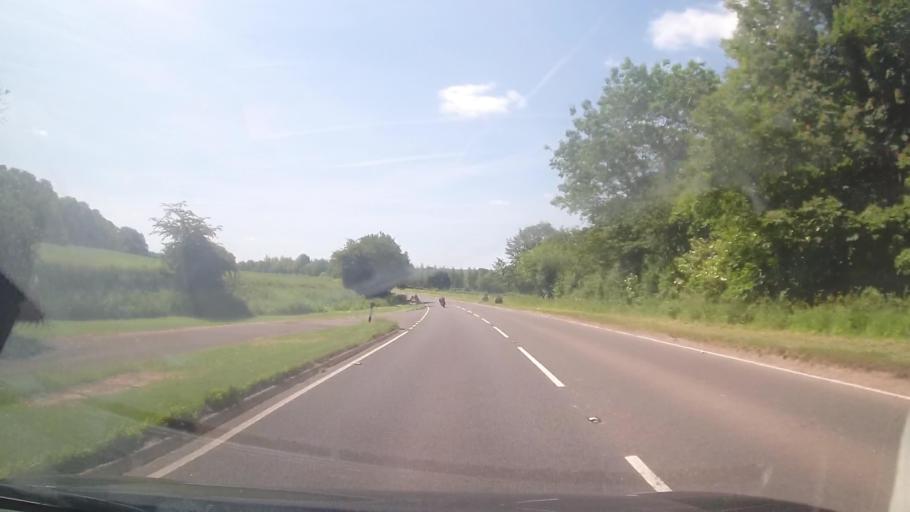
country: GB
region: England
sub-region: Herefordshire
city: Kimbolton
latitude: 52.2541
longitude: -2.7188
